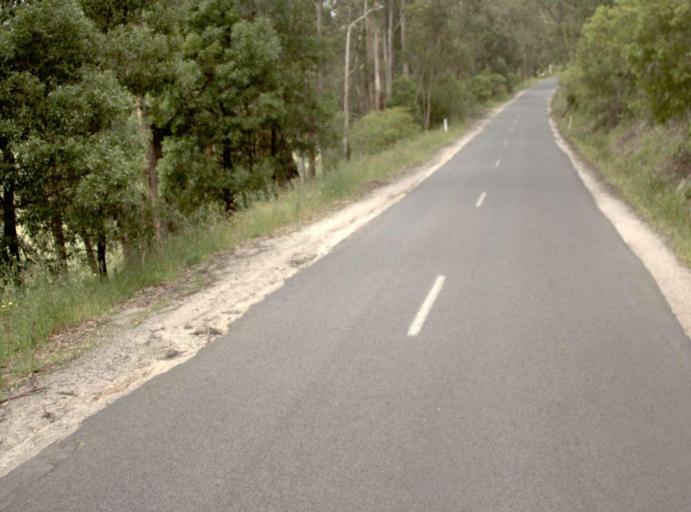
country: AU
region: Victoria
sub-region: Latrobe
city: Moe
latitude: -37.9846
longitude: 146.1439
